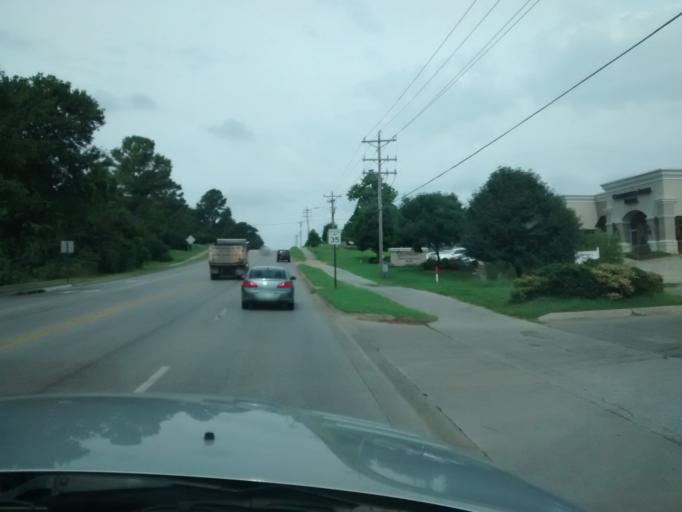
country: US
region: Arkansas
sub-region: Washington County
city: Johnson
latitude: 36.1199
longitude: -94.1199
